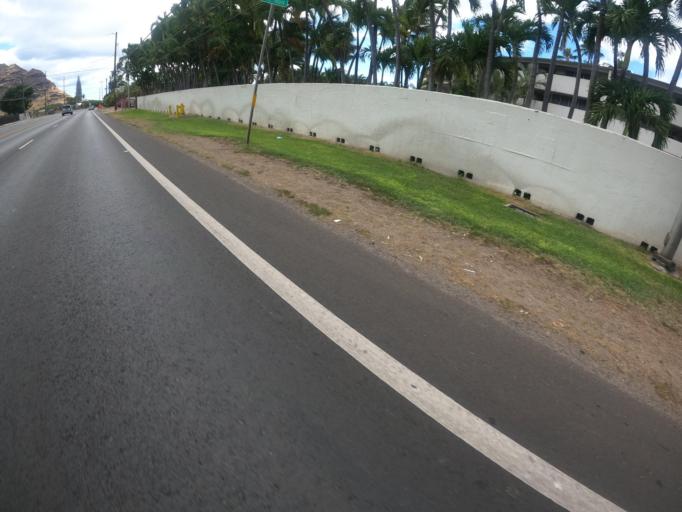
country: US
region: Hawaii
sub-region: Honolulu County
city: Ma'ili
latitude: 21.4146
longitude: -158.1768
